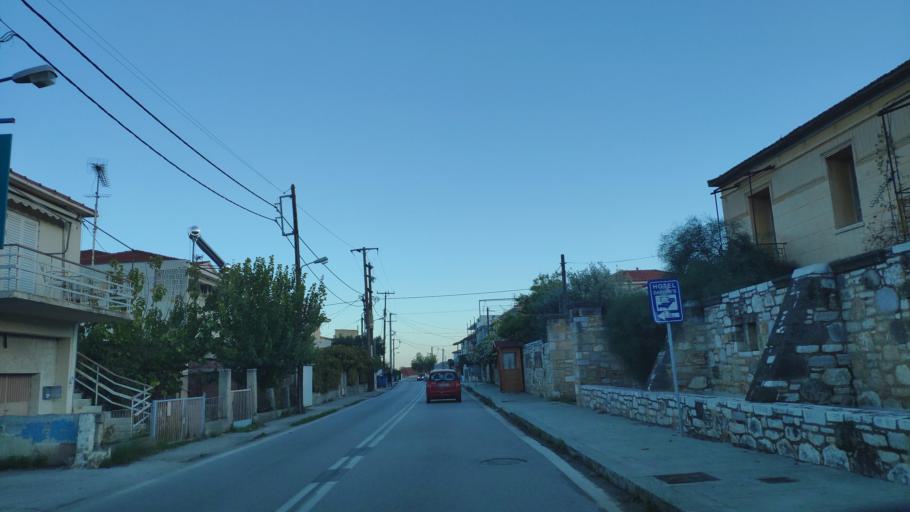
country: GR
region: Peloponnese
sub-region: Nomos Korinthias
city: Xylokastro
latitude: 38.0681
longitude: 22.6549
